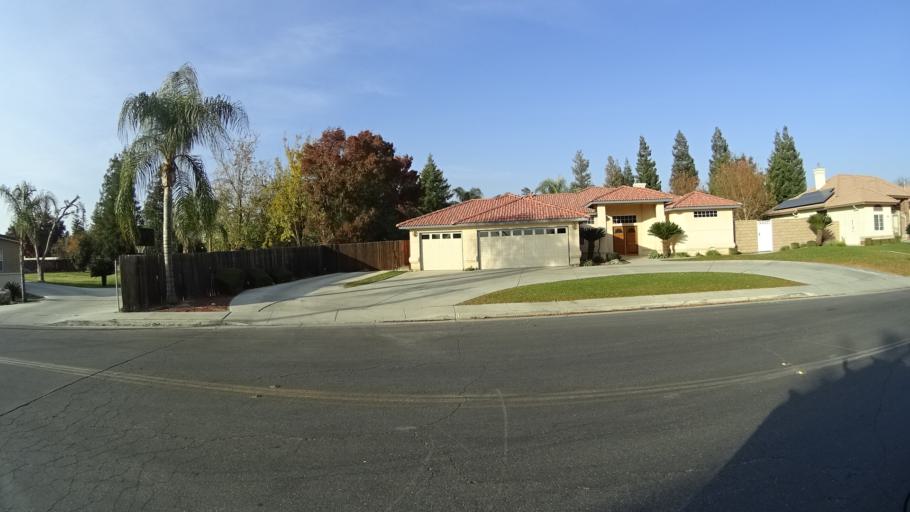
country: US
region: California
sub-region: Kern County
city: Greenacres
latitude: 35.3726
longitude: -119.1236
